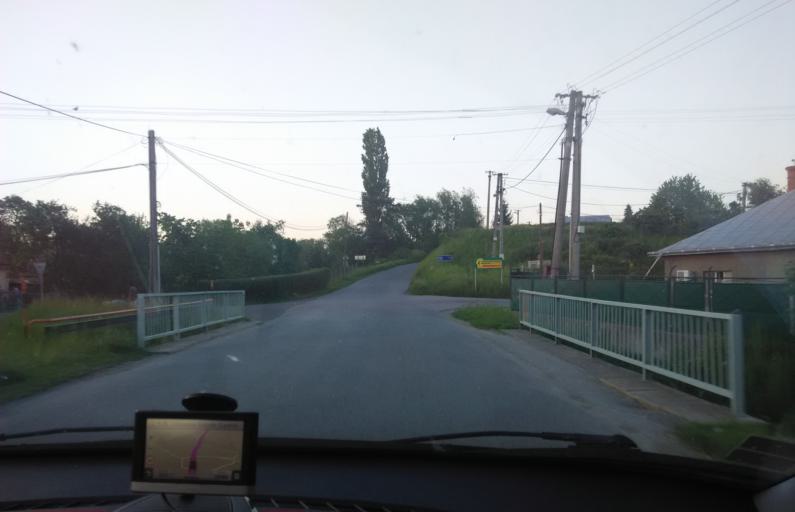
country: SK
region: Presovsky
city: Sabinov
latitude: 49.0610
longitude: 21.0624
